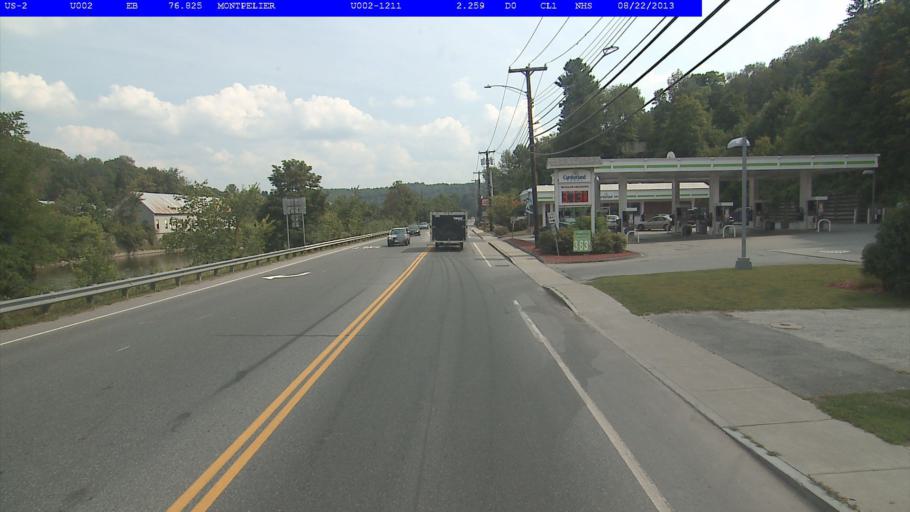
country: US
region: Vermont
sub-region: Washington County
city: Montpelier
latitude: 44.2566
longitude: -72.5766
